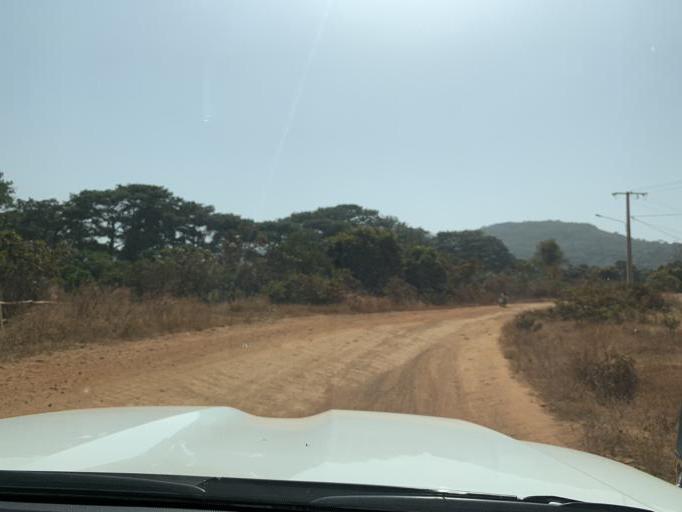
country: GN
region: Mamou
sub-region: Dalaba
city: Dalaba
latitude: 10.7265
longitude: -12.2455
